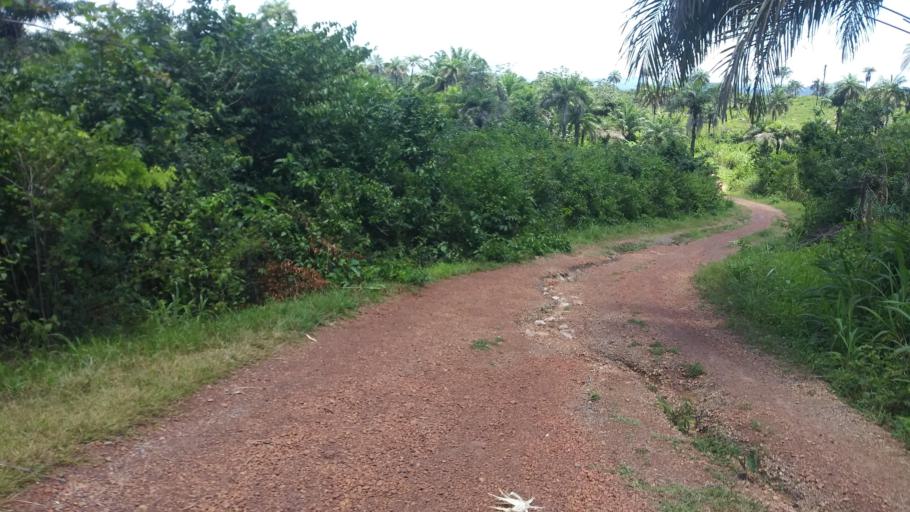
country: SL
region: Northern Province
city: Binkolo
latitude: 8.9097
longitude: -11.9830
